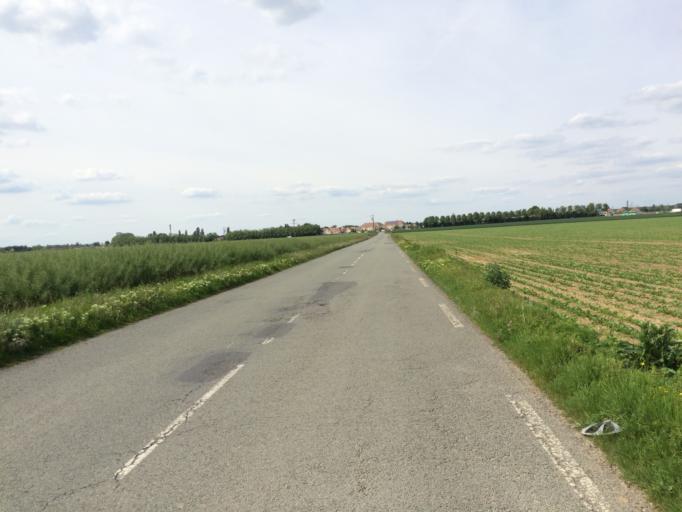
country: FR
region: Ile-de-France
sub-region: Departement de l'Essonne
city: Saclay
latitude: 48.7233
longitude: 2.1798
